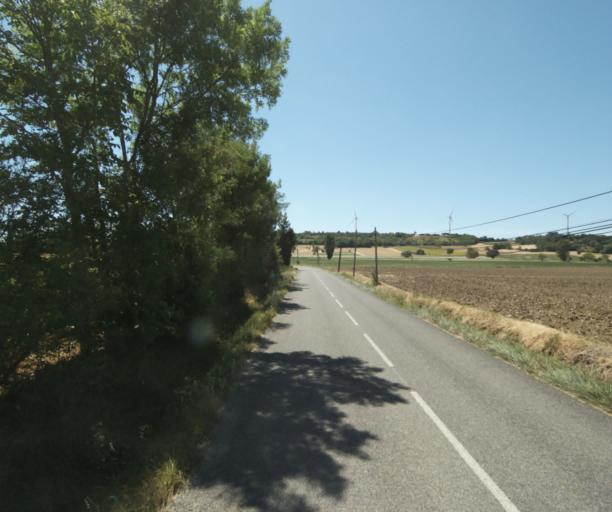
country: FR
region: Midi-Pyrenees
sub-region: Departement de la Haute-Garonne
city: Saint-Felix-Lauragais
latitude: 43.4712
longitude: 1.9293
